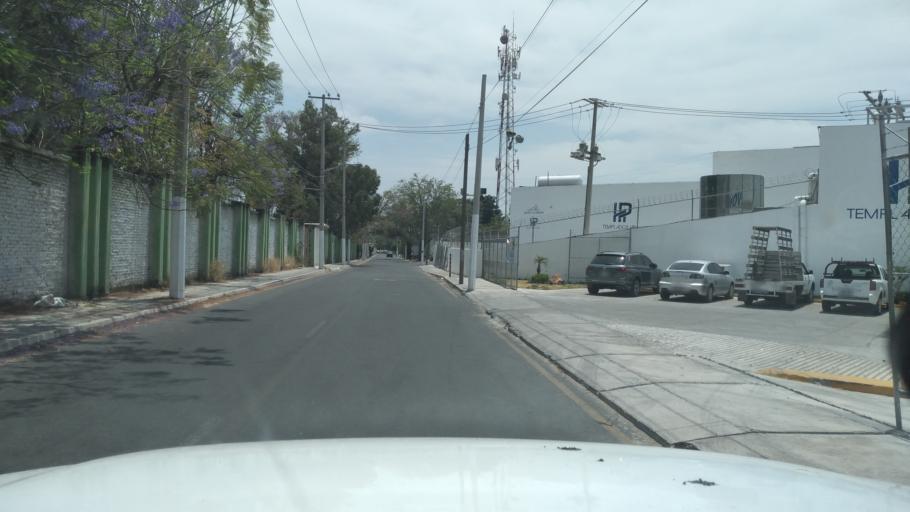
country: MX
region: Jalisco
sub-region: Zapopan
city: Zapopan
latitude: 20.7340
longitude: -103.3726
